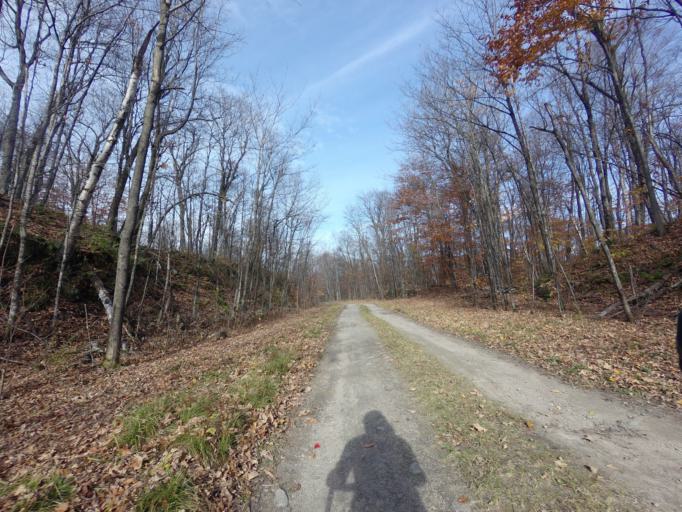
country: CA
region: Quebec
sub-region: Outaouais
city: Wakefield
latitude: 45.5240
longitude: -75.9277
